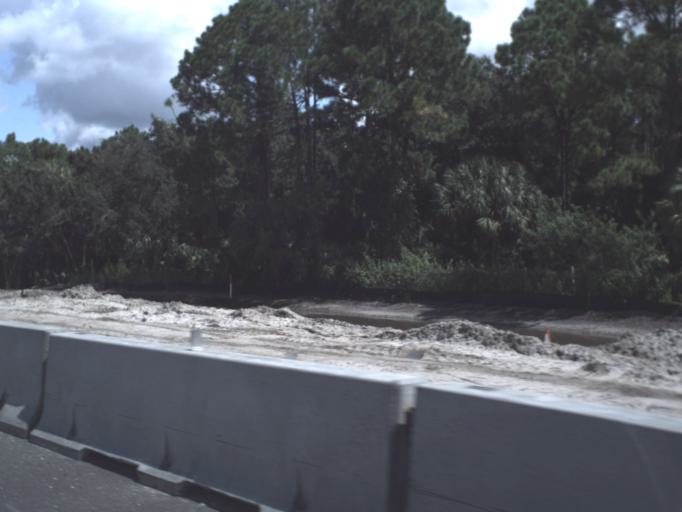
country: US
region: Florida
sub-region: Sarasota County
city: The Meadows
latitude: 27.3961
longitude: -82.4507
